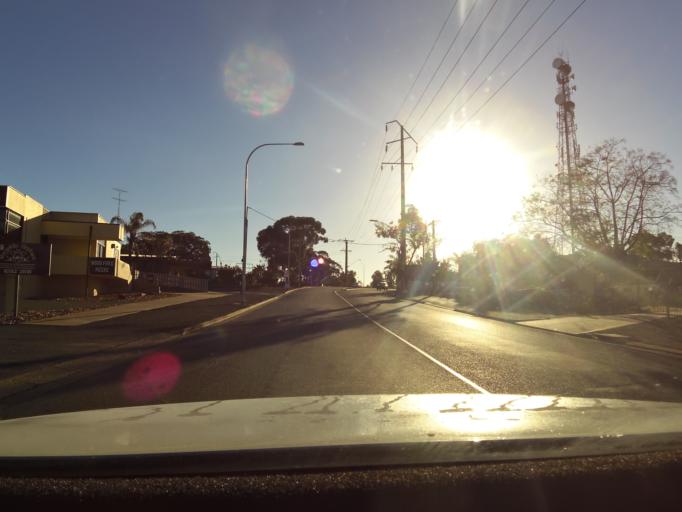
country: AU
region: South Australia
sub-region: Berri and Barmera
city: Berri
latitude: -34.2831
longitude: 140.5967
